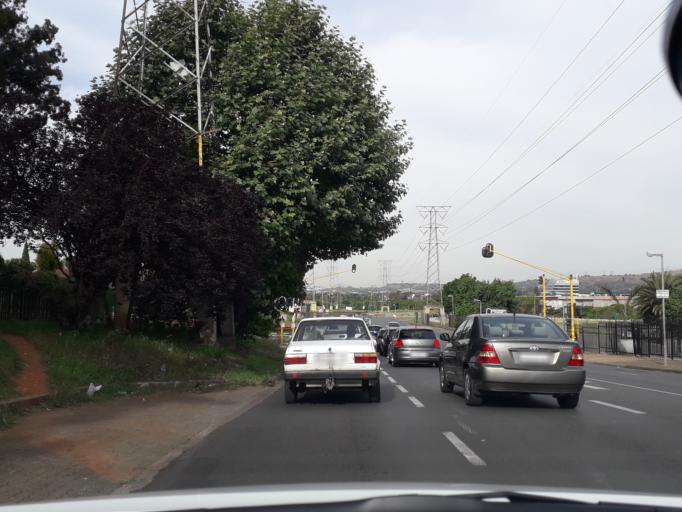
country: ZA
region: Gauteng
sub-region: City of Johannesburg Metropolitan Municipality
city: Johannesburg
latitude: -26.1783
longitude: 28.1057
